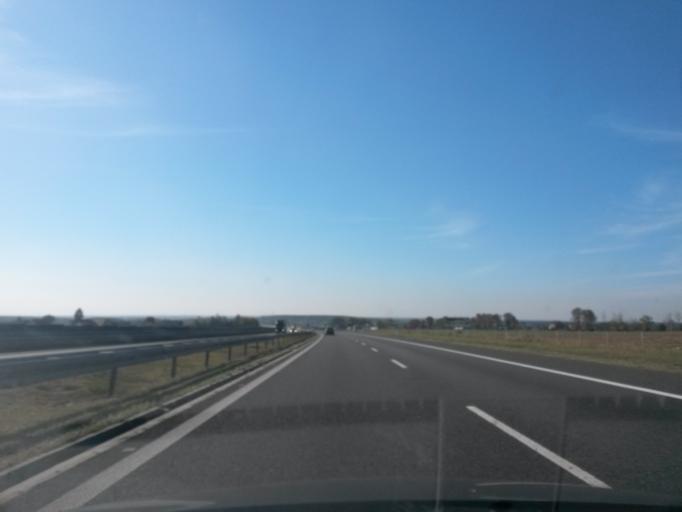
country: PL
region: Opole Voivodeship
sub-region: Powiat krapkowicki
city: Gogolin
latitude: 50.4832
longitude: 18.0467
